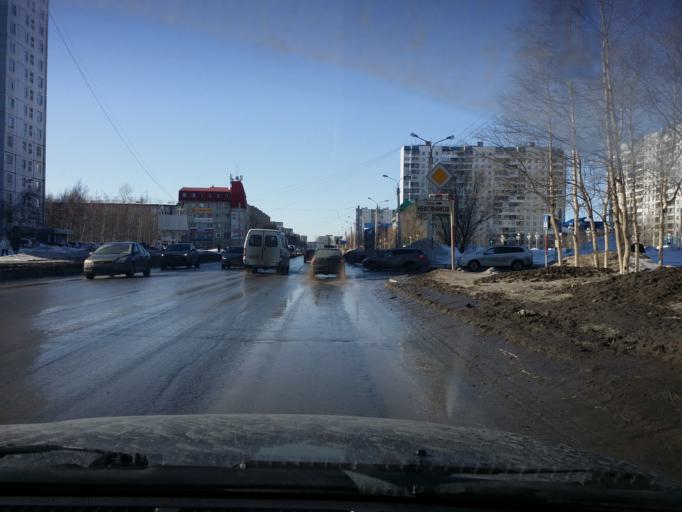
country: RU
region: Khanty-Mansiyskiy Avtonomnyy Okrug
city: Nizhnevartovsk
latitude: 60.9418
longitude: 76.5839
